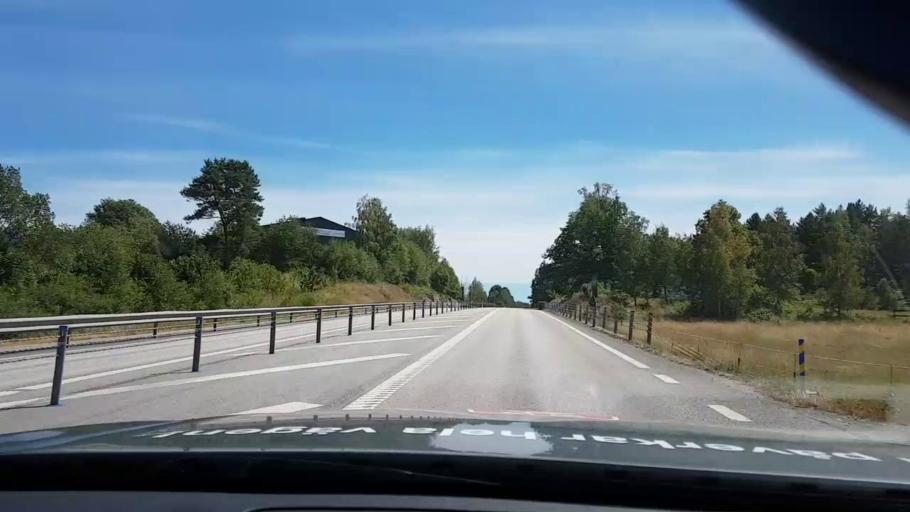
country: SE
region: Kalmar
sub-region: Vasterviks Kommun
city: Gamleby
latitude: 57.8700
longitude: 16.4118
